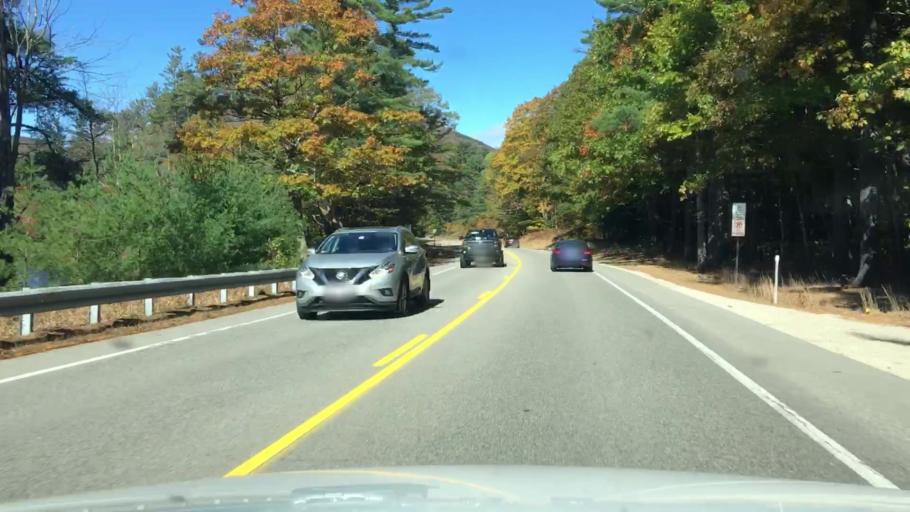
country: US
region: New Hampshire
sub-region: Carroll County
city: Tamworth
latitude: 43.9075
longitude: -71.2333
